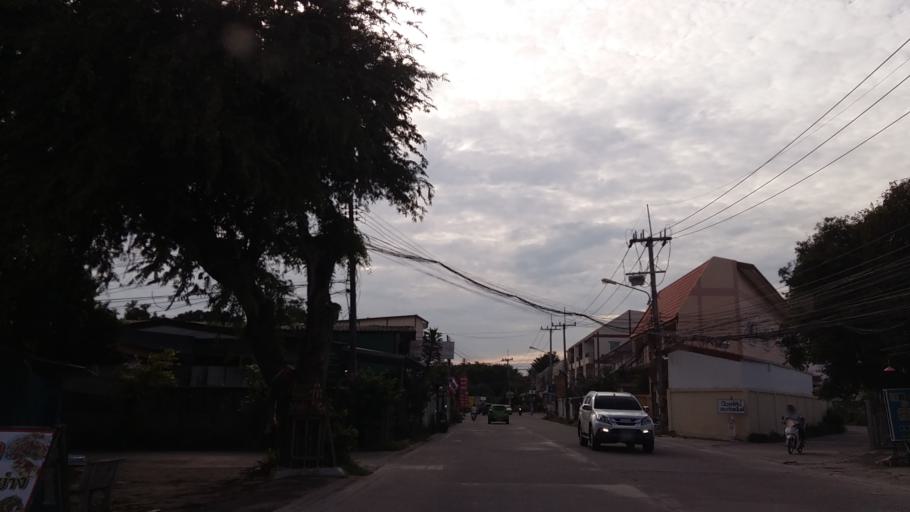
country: TH
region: Chon Buri
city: Chon Buri
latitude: 13.3188
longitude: 100.9463
